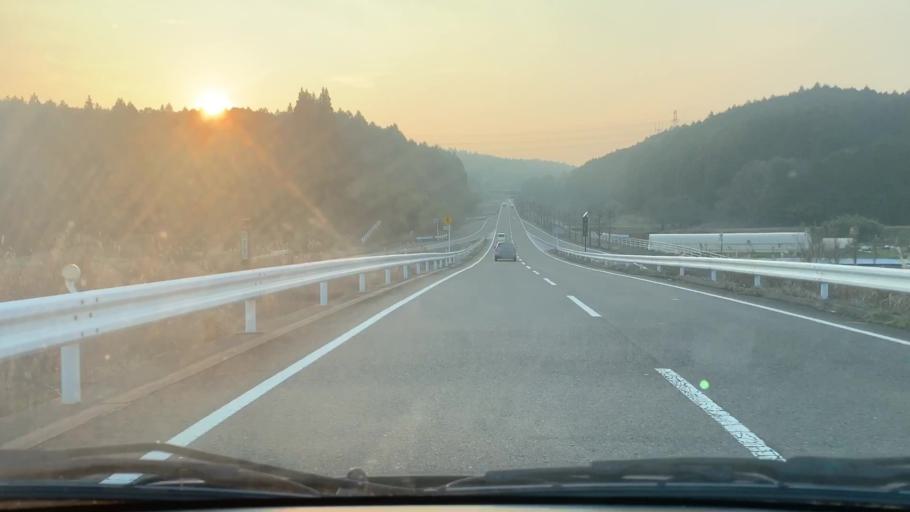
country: JP
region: Saga Prefecture
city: Imaricho-ko
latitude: 33.2603
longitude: 129.9311
